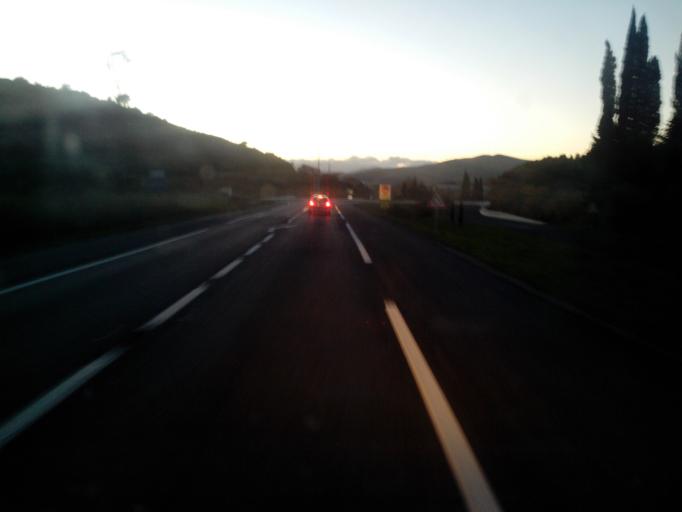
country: FR
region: Languedoc-Roussillon
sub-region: Departement des Pyrenees-Orientales
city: Estagel
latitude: 42.7754
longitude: 2.7112
